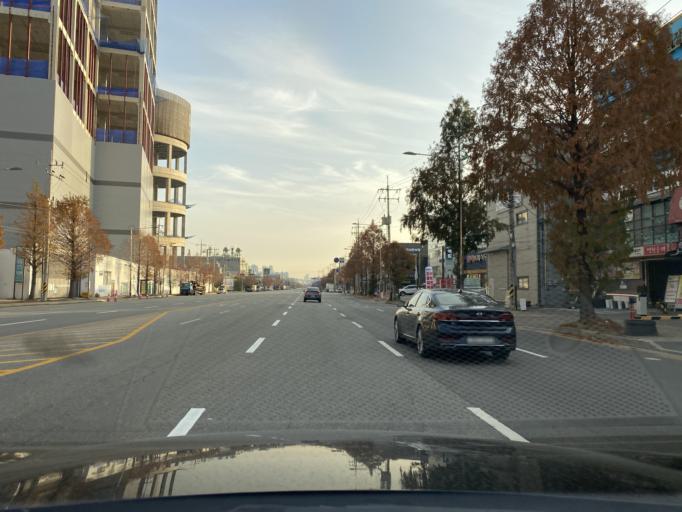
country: KR
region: Incheon
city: Incheon
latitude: 37.5055
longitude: 126.6617
